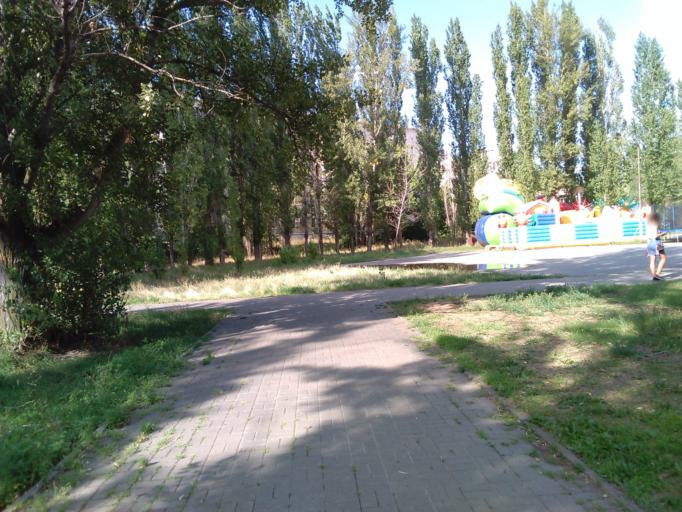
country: RU
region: Rostov
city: Bataysk
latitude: 47.1302
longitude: 39.7374
